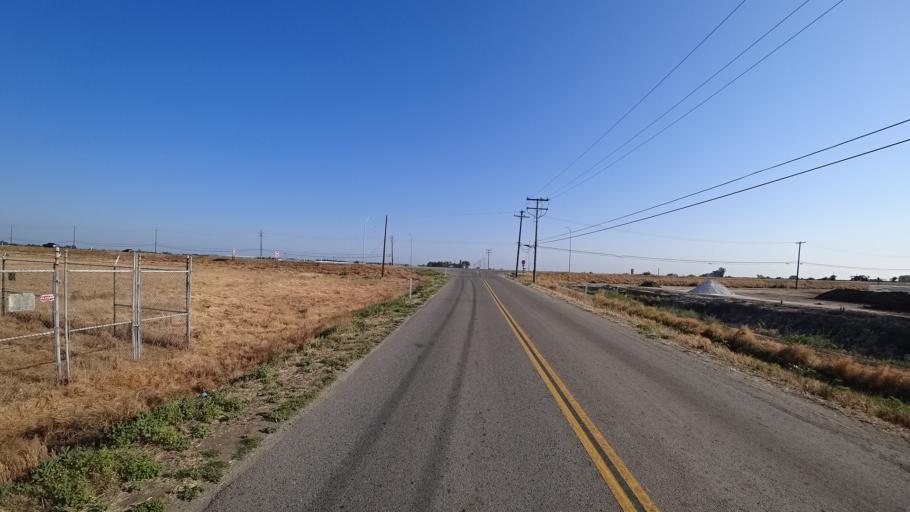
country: US
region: California
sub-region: Kings County
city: Home Garden
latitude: 36.3275
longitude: -119.5652
